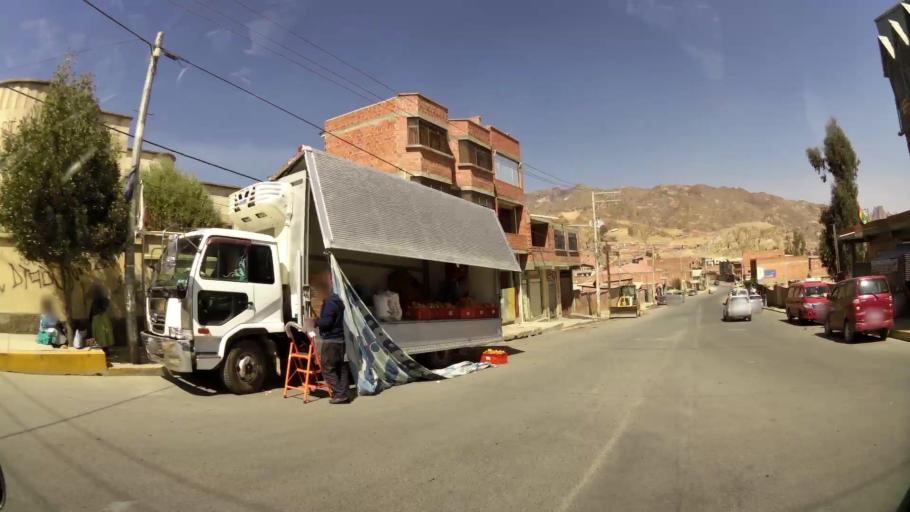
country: BO
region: La Paz
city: La Paz
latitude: -16.5337
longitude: -68.0366
